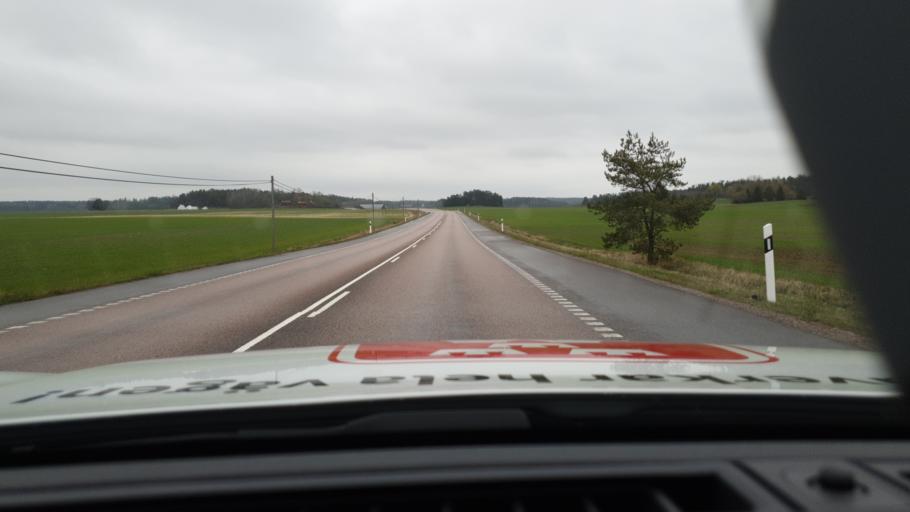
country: SE
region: Soedermanland
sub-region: Trosa Kommun
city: Vagnharad
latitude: 59.0212
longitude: 17.5924
